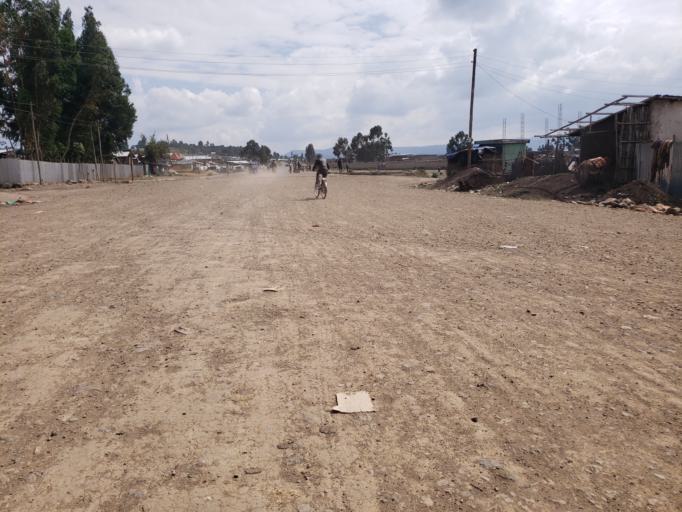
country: ET
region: Oromiya
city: Dodola
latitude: 7.0020
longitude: 39.3917
